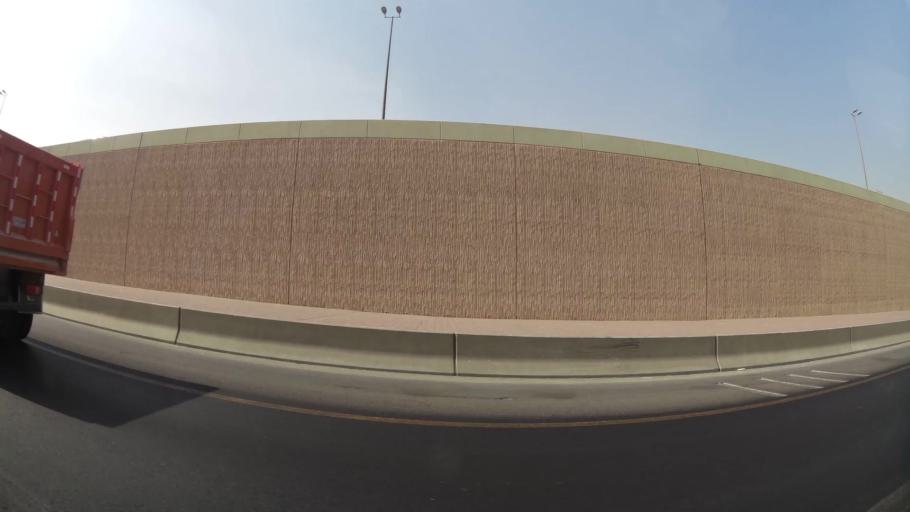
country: KW
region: Al Farwaniyah
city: Al Farwaniyah
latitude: 29.2777
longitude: 47.9499
